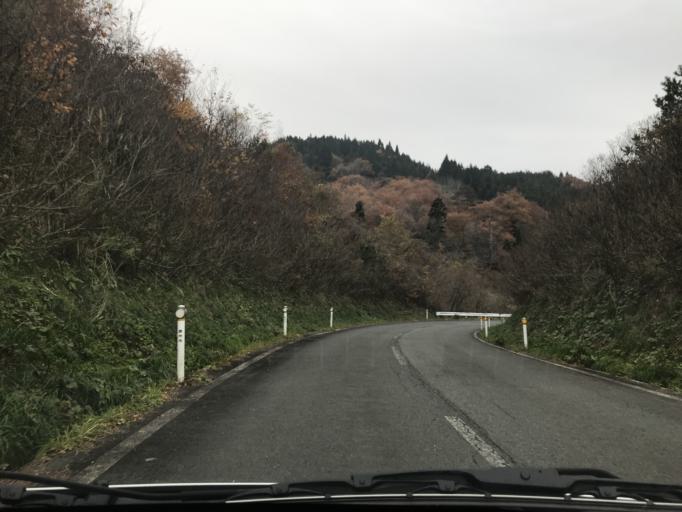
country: JP
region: Iwate
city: Ichinoseki
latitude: 39.0161
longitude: 141.0740
